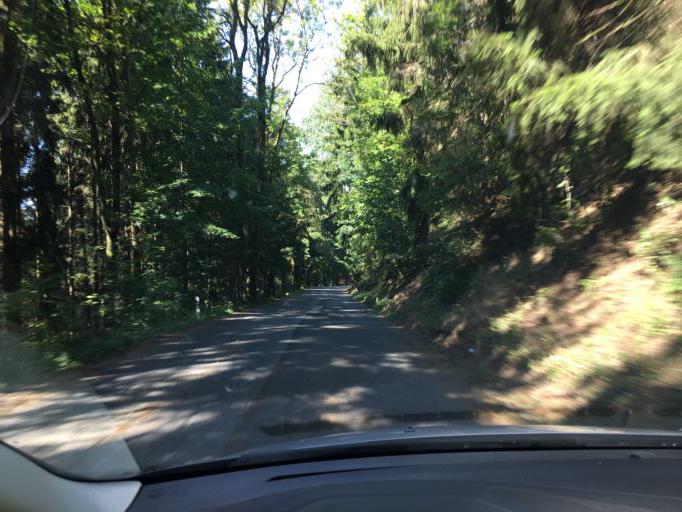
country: CZ
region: Liberecky
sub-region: Okres Semily
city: Vysoke nad Jizerou
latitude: 50.7016
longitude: 15.3696
